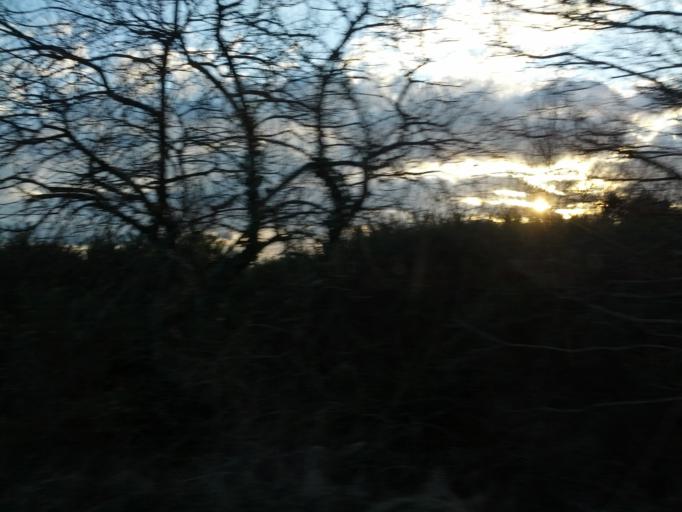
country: IE
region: Connaught
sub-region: County Galway
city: Athenry
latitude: 53.3315
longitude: -8.7001
